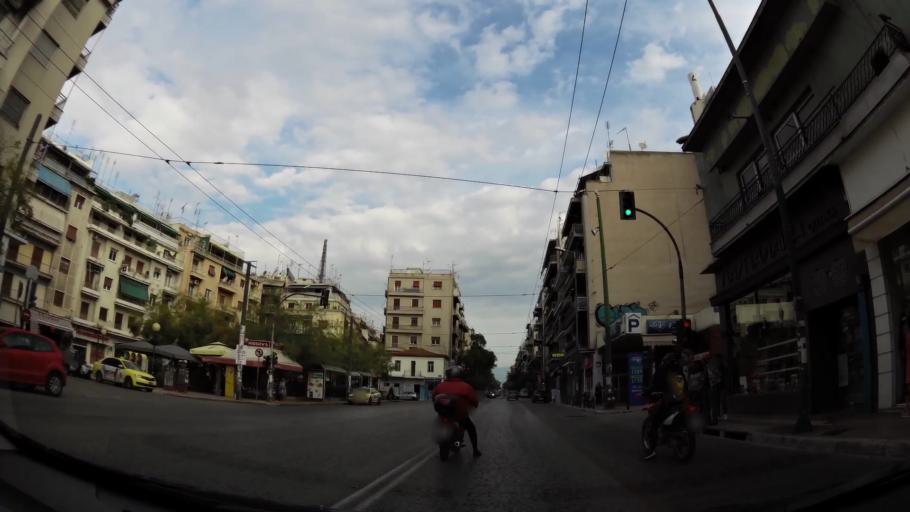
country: GR
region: Attica
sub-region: Nomarchia Athinas
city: Kipseli
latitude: 38.0098
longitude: 23.7351
